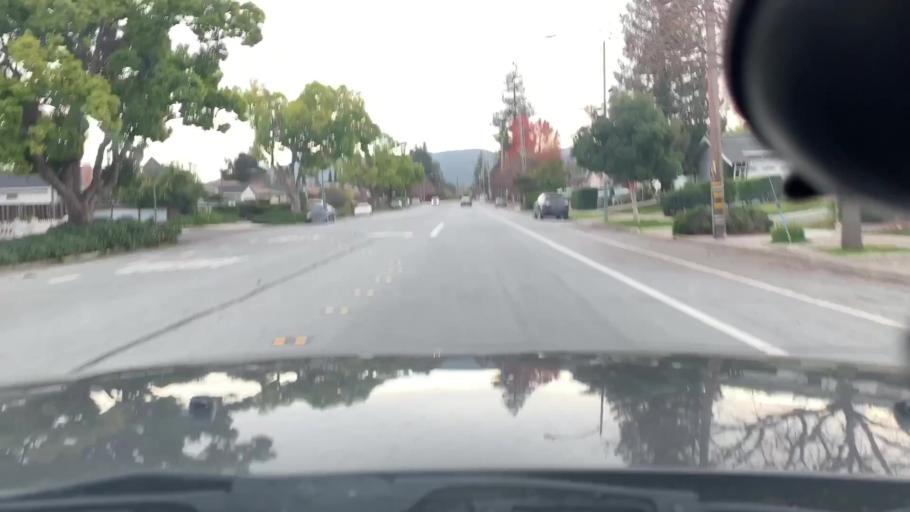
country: US
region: California
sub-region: Santa Clara County
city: Cupertino
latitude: 37.3061
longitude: -122.0415
